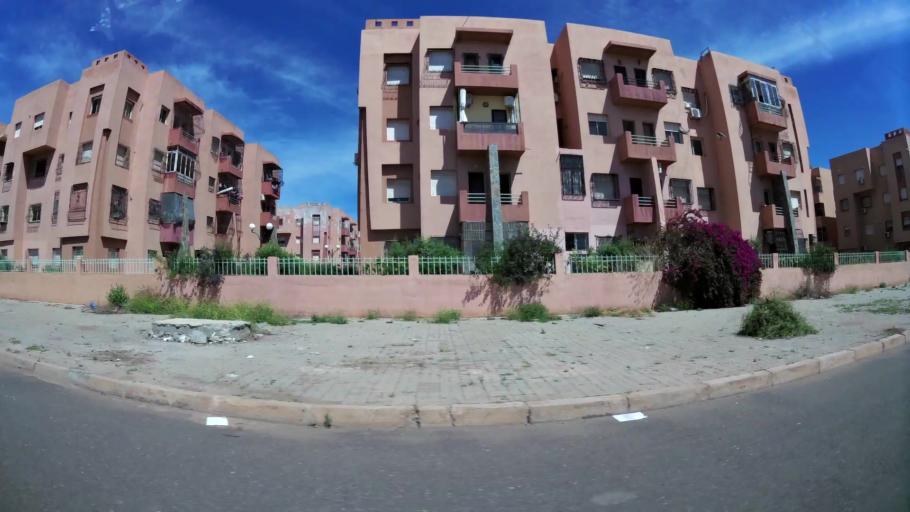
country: MA
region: Marrakech-Tensift-Al Haouz
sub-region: Marrakech
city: Marrakesh
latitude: 31.6457
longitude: -8.0815
